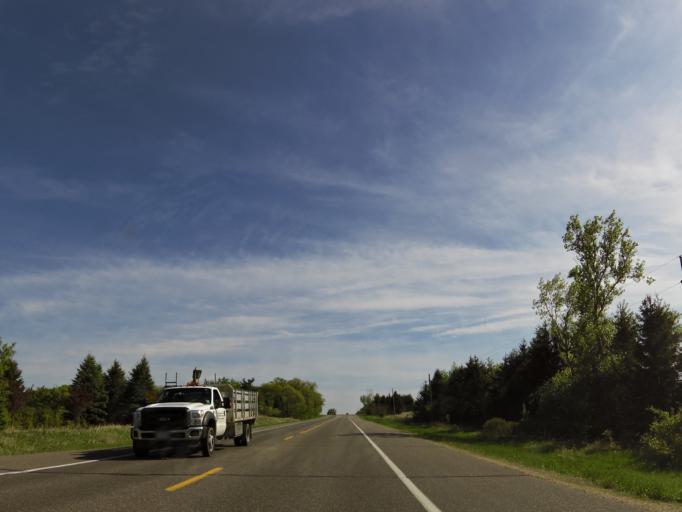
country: US
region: Minnesota
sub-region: Washington County
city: Oakdale
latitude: 44.9741
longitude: -92.9338
